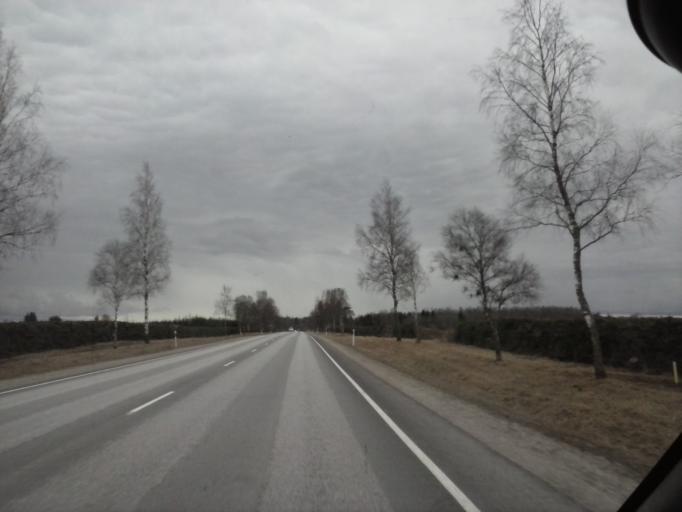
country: EE
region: Jaervamaa
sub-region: Paide linn
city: Paide
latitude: 58.9970
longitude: 25.5938
